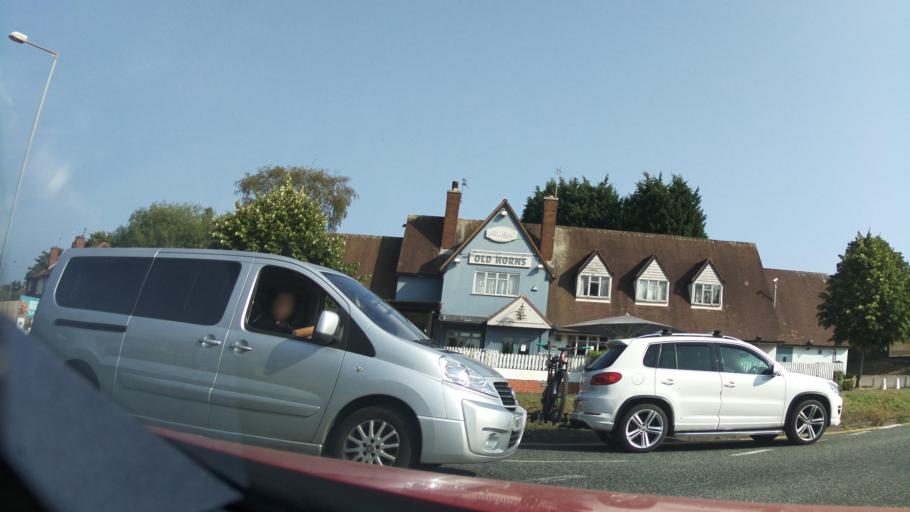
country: GB
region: England
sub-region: Walsall
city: Streetly
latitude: 52.5532
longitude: -1.9094
